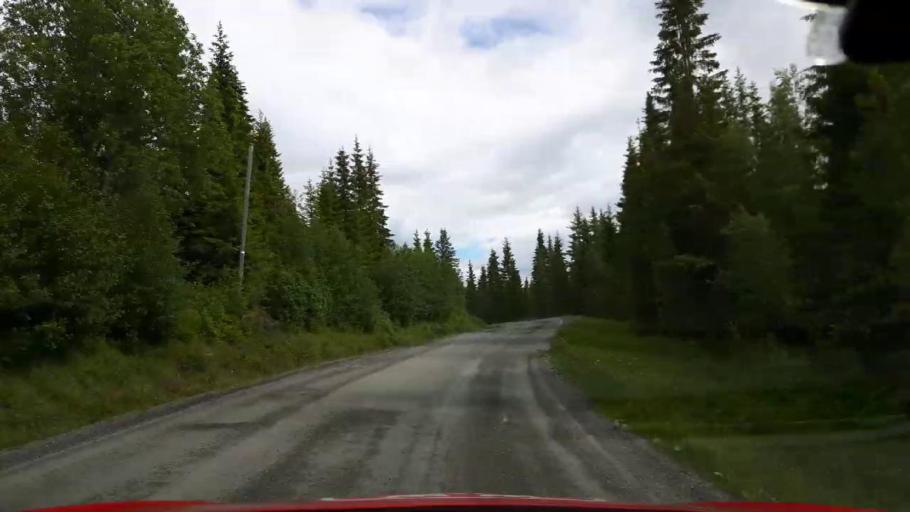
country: NO
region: Nord-Trondelag
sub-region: Lierne
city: Sandvika
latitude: 64.1445
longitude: 13.9087
